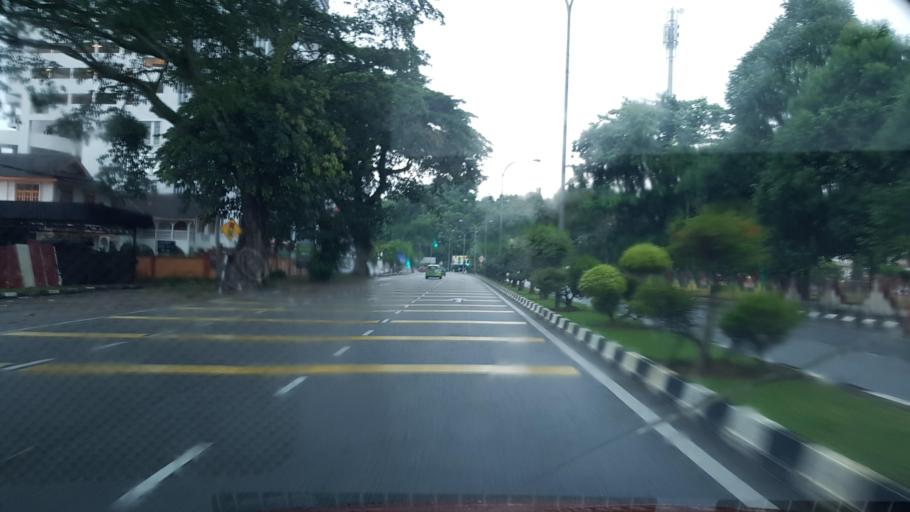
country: MY
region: Terengganu
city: Kuala Terengganu
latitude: 5.3232
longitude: 103.1417
